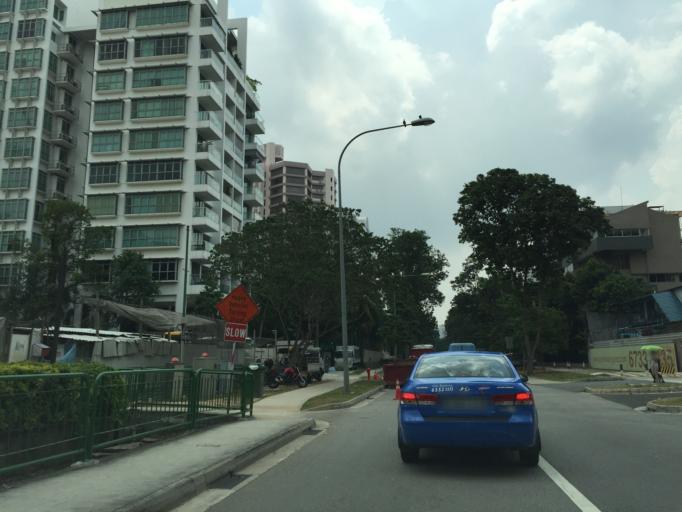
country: SG
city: Singapore
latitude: 1.3153
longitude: 103.8327
